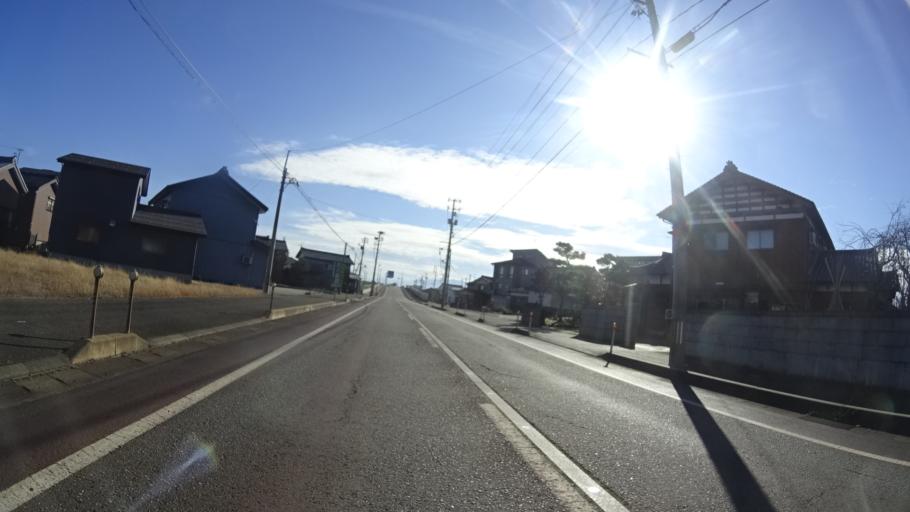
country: JP
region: Niigata
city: Mitsuke
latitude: 37.5470
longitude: 138.8783
